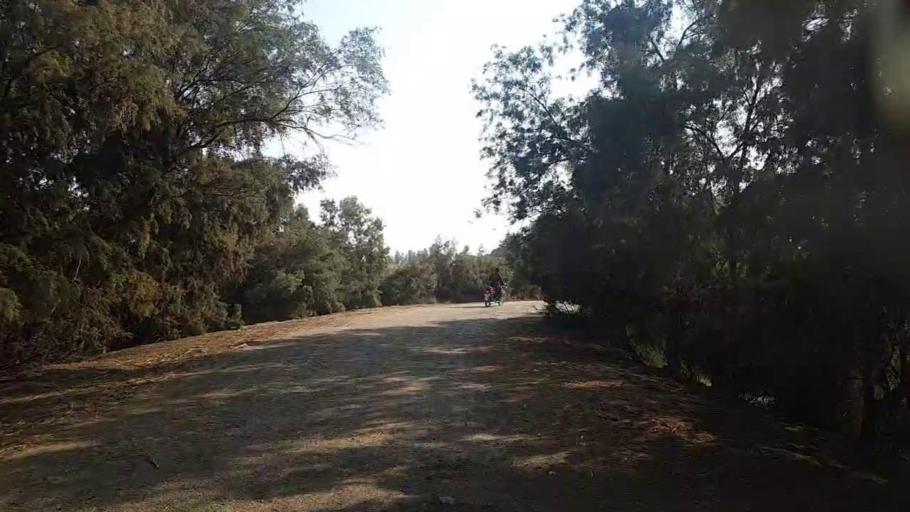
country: PK
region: Sindh
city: Mirpur Mathelo
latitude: 27.8964
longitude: 69.6070
